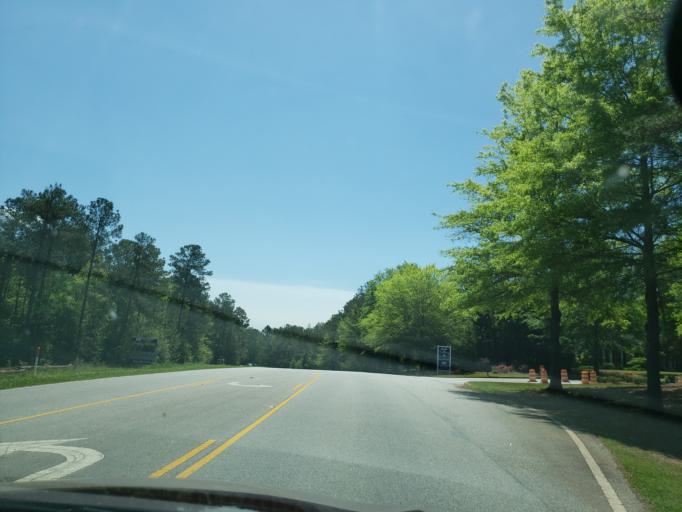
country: US
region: Alabama
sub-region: Lee County
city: Auburn
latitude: 32.6513
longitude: -85.5154
